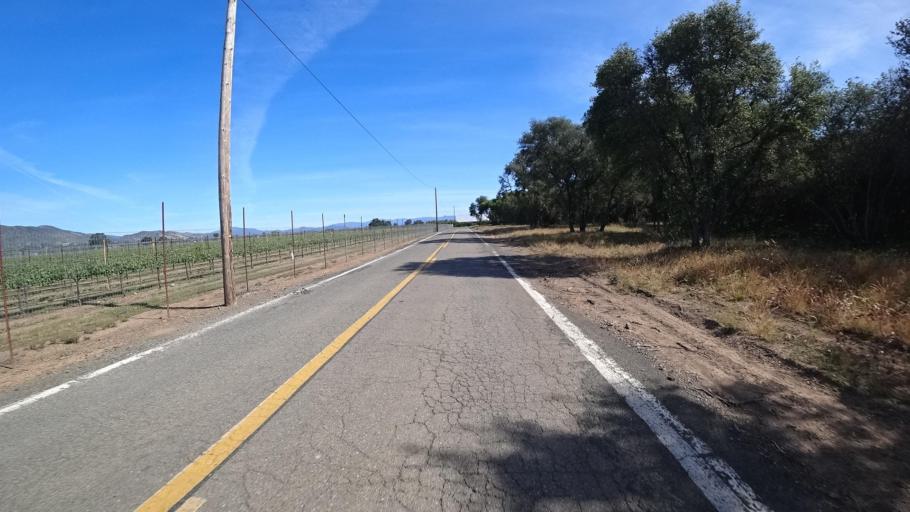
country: US
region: California
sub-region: Lake County
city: Kelseyville
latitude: 38.9626
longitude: -122.8810
